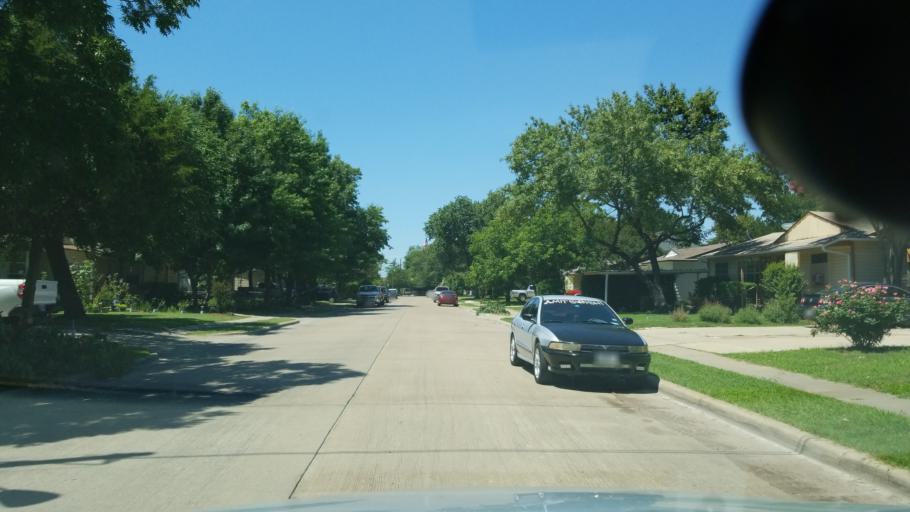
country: US
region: Texas
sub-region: Dallas County
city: Irving
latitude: 32.8334
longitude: -96.9323
